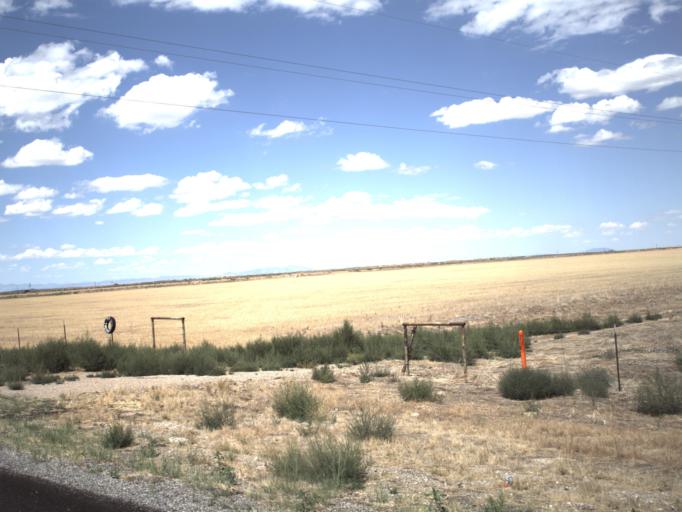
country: US
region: Utah
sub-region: Millard County
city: Fillmore
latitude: 39.1181
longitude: -112.3460
